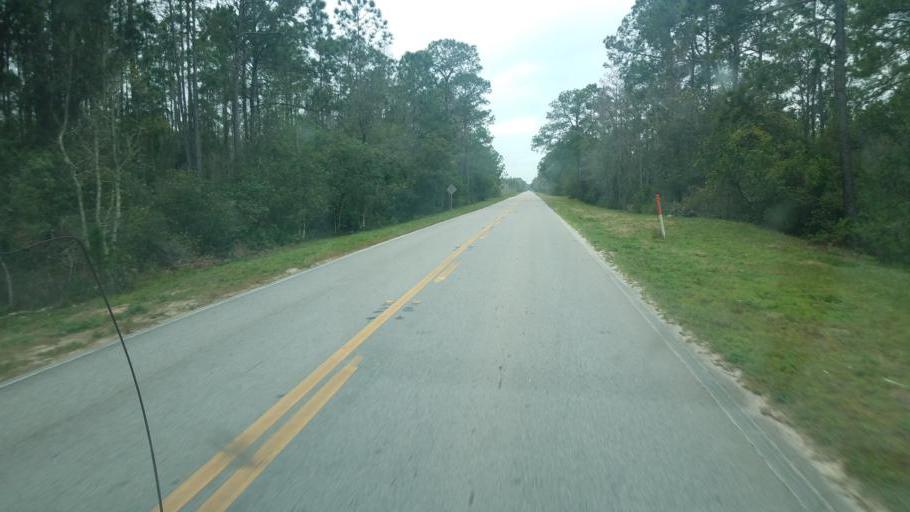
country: US
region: Florida
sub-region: Polk County
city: Polk City
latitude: 28.2564
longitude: -81.7393
